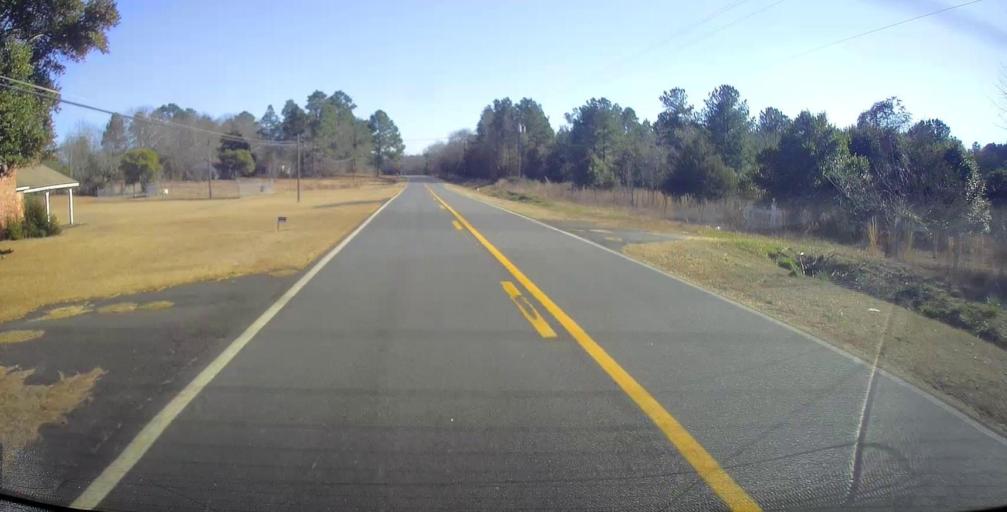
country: US
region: Georgia
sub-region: Taylor County
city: Butler
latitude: 32.5473
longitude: -84.2277
